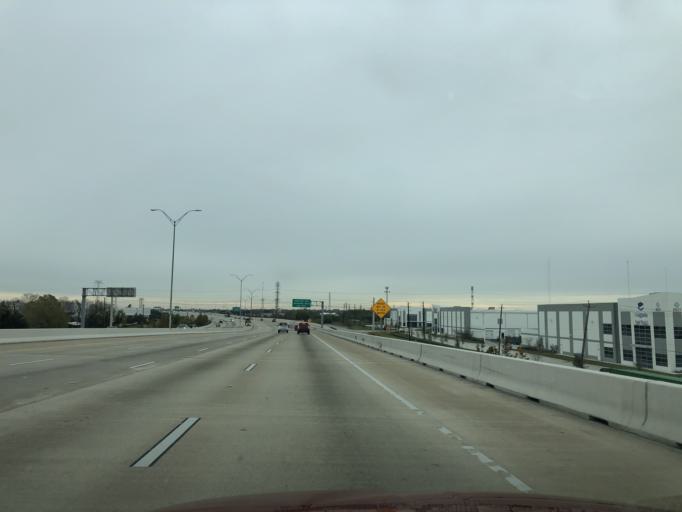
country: US
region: Texas
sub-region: Fort Bend County
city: Missouri City
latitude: 29.6253
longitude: -95.5168
